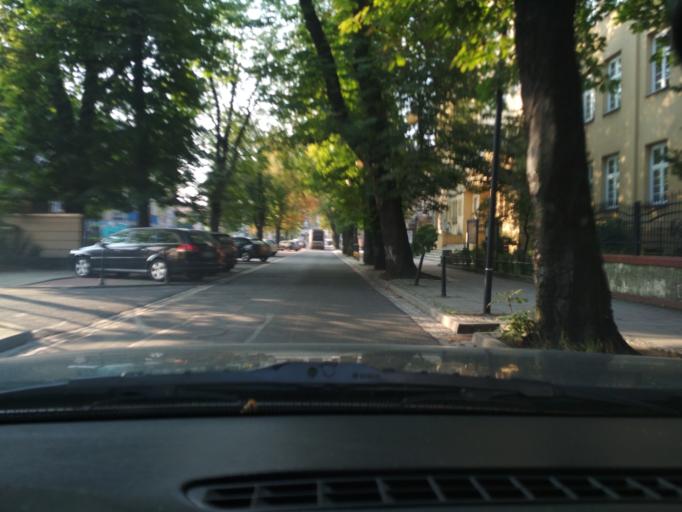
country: PL
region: Silesian Voivodeship
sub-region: Gliwice
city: Gliwice
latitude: 50.2975
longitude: 18.6733
